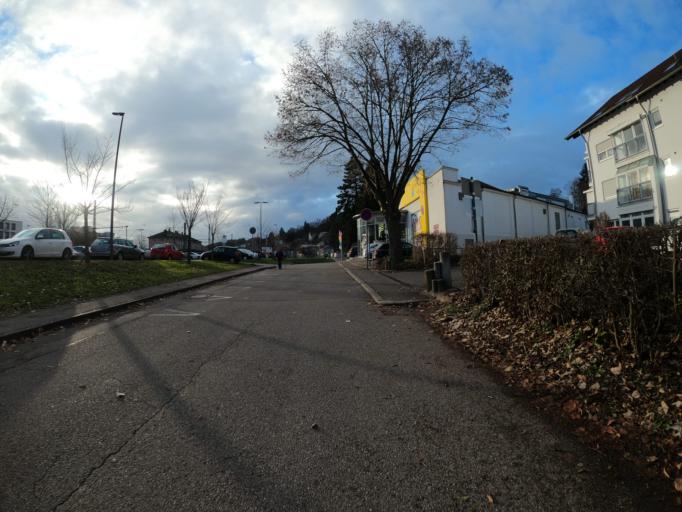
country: DE
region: Baden-Wuerttemberg
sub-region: Regierungsbezirk Stuttgart
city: Schwabisch Gmund
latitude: 48.8019
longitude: 9.7902
